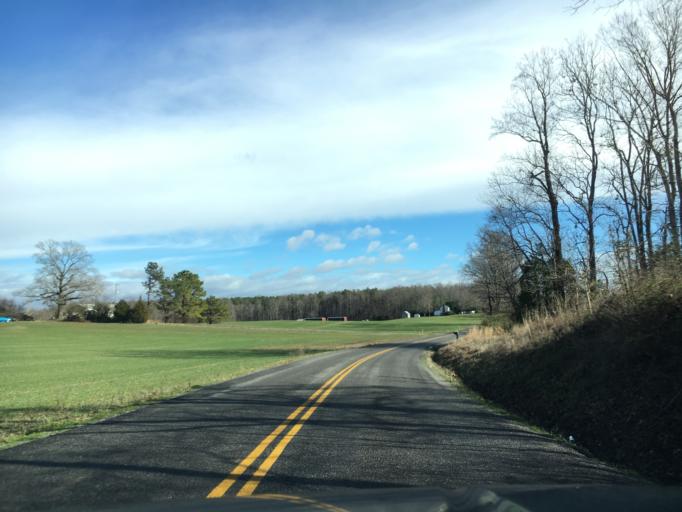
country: US
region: Virginia
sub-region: Amelia County
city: Amelia Court House
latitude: 37.4347
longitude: -78.0492
